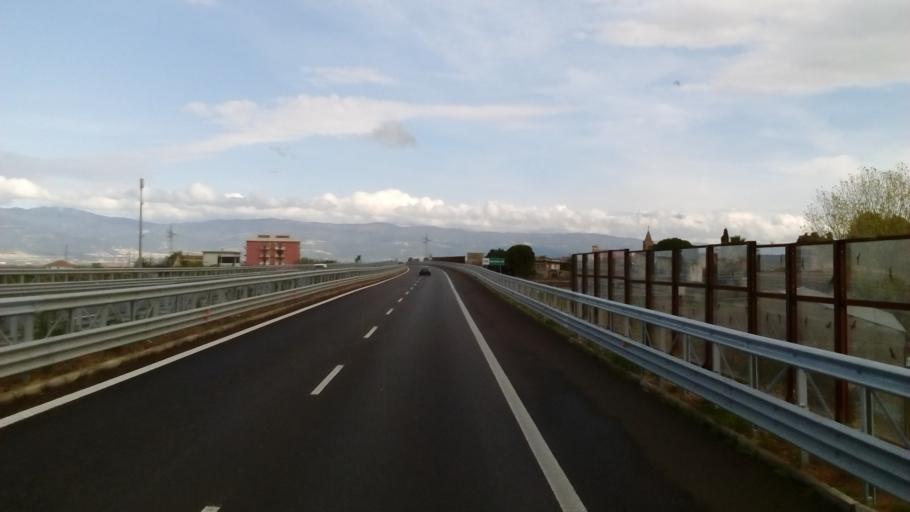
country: IT
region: Calabria
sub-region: Provincia di Catanzaro
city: Acconia
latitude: 38.8369
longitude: 16.2596
